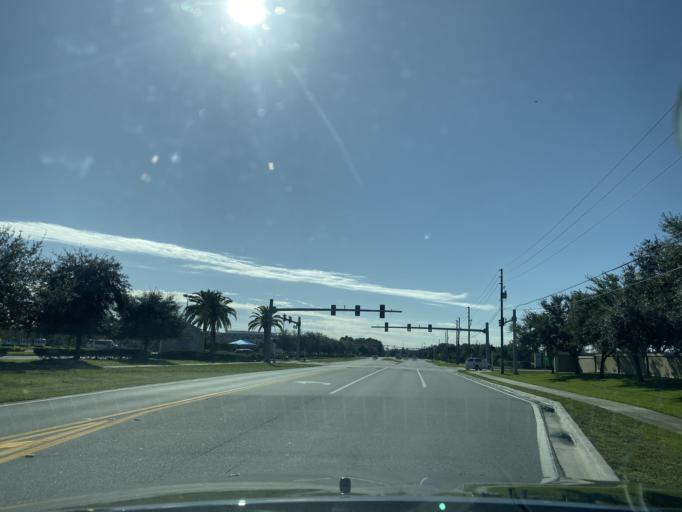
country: US
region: Florida
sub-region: Orange County
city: Azalea Park
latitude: 28.5130
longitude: -81.2566
